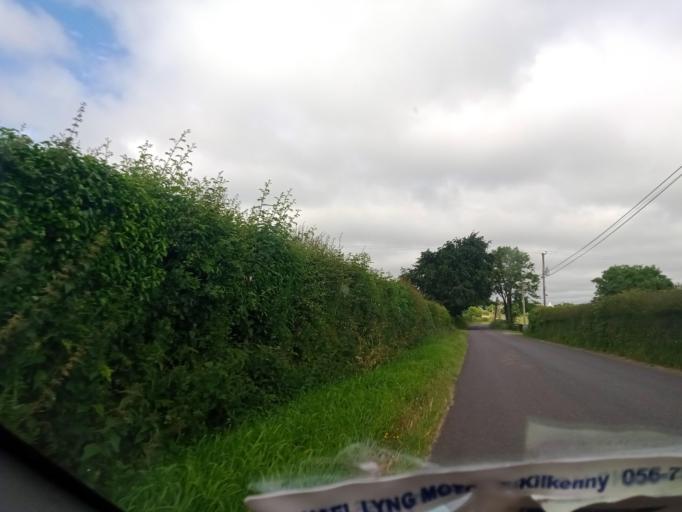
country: IE
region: Leinster
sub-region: Kilkenny
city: Ballyragget
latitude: 52.7645
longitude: -7.4634
